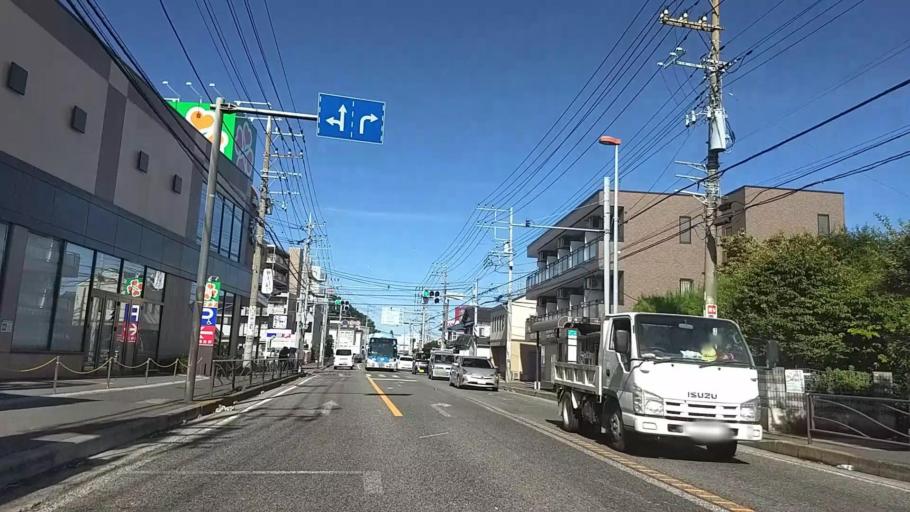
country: JP
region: Kanagawa
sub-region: Kawasaki-shi
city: Kawasaki
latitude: 35.5648
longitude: 139.6415
